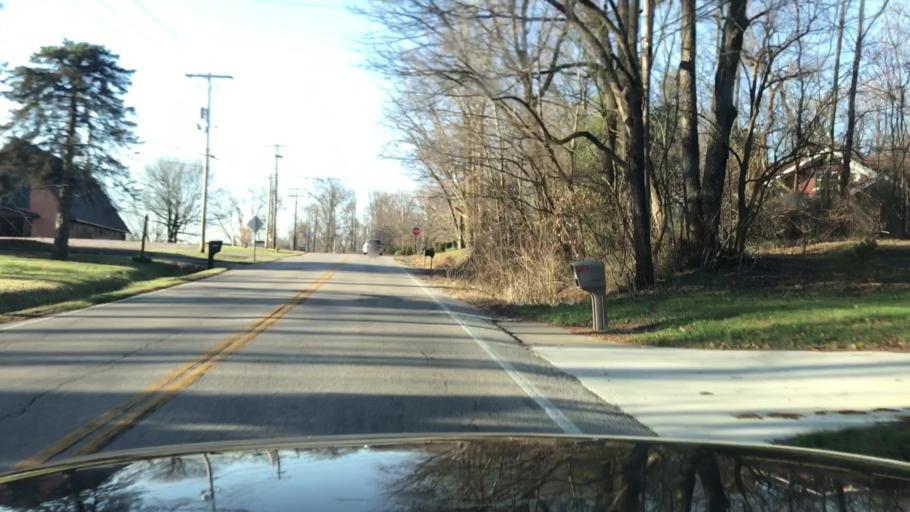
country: US
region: Indiana
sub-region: Vanderburgh County
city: Highland
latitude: 38.0365
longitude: -87.5639
